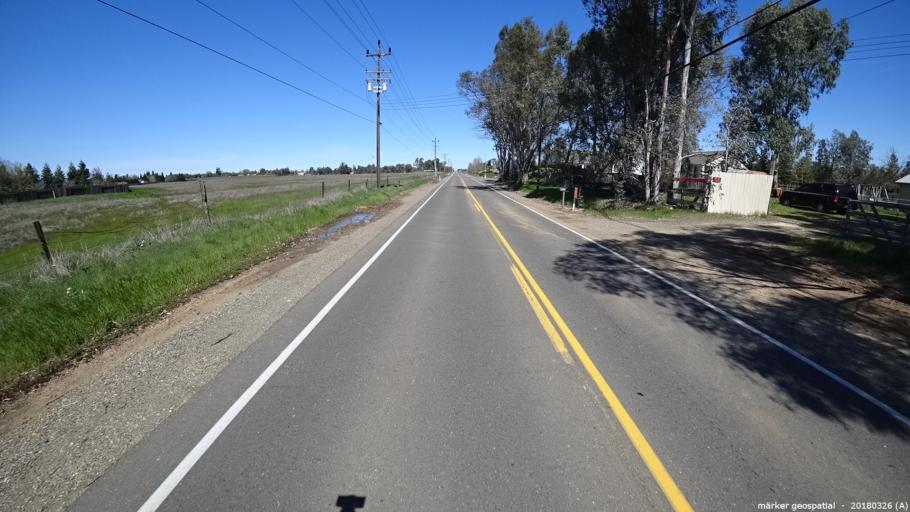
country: US
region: California
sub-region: Sacramento County
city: Vineyard
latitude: 38.4625
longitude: -121.2976
